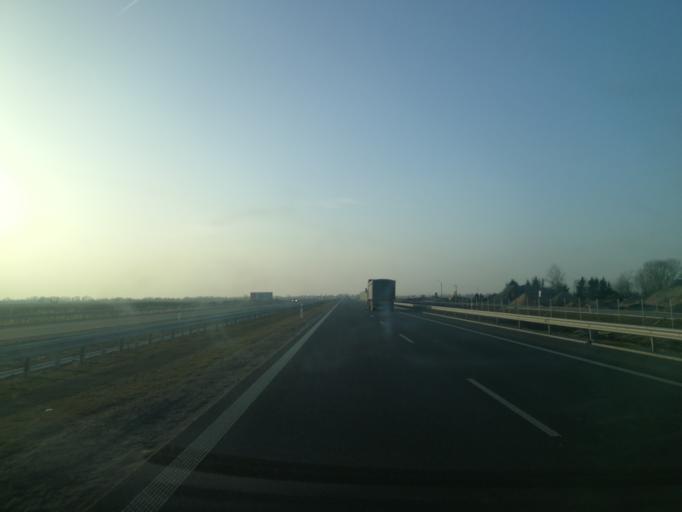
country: PL
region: Pomeranian Voivodeship
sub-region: Powiat nowodworski
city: Ostaszewo
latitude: 54.2376
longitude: 19.0271
